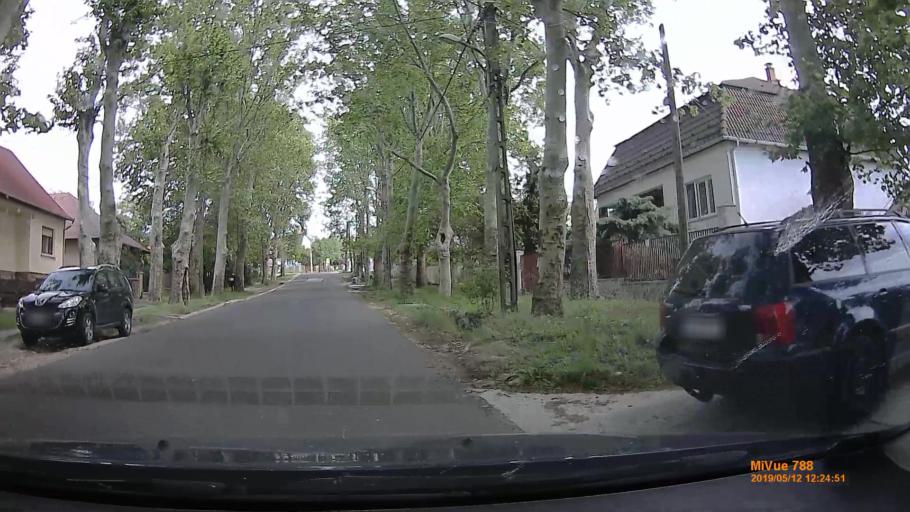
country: HU
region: Pest
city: Ecser
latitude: 47.4589
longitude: 19.2985
